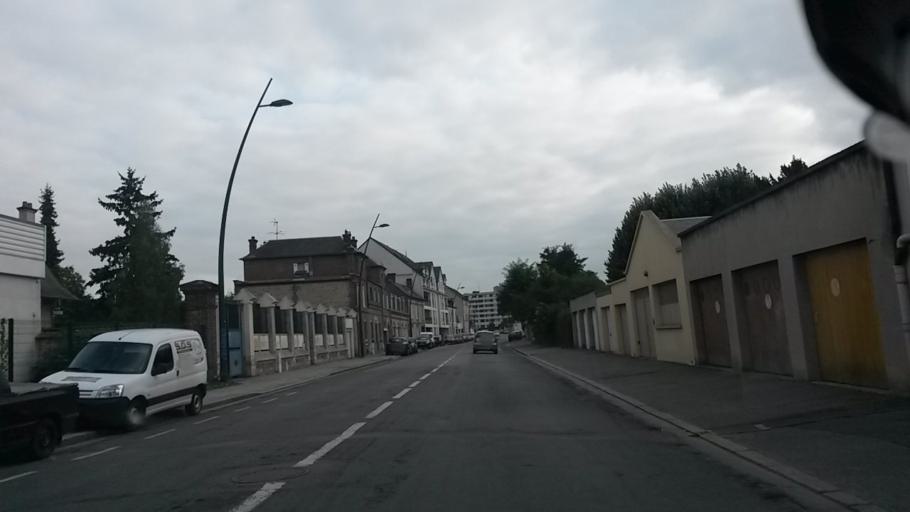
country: FR
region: Haute-Normandie
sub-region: Departement de l'Eure
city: Evreux
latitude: 49.0315
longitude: 1.1565
